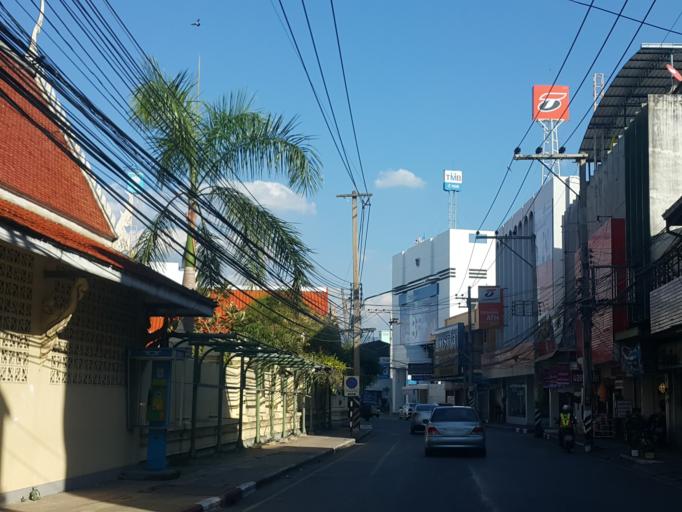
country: TH
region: Lampang
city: Lampang
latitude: 18.2886
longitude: 99.4958
